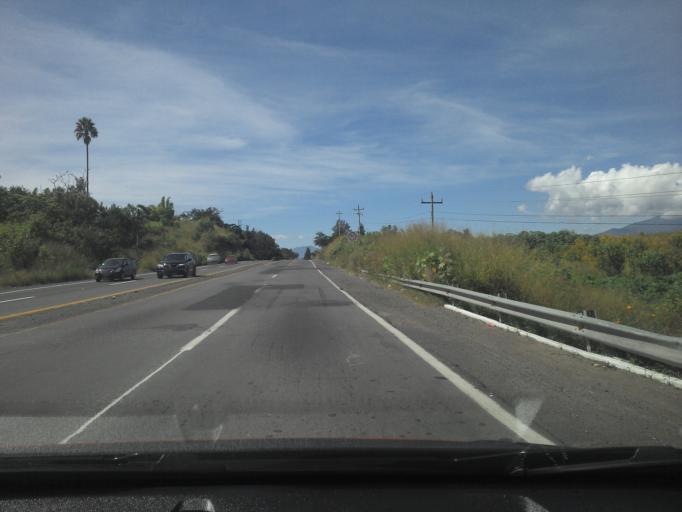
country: MX
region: Jalisco
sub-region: Tala
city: Los Ruisenores
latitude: 20.7194
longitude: -103.6305
